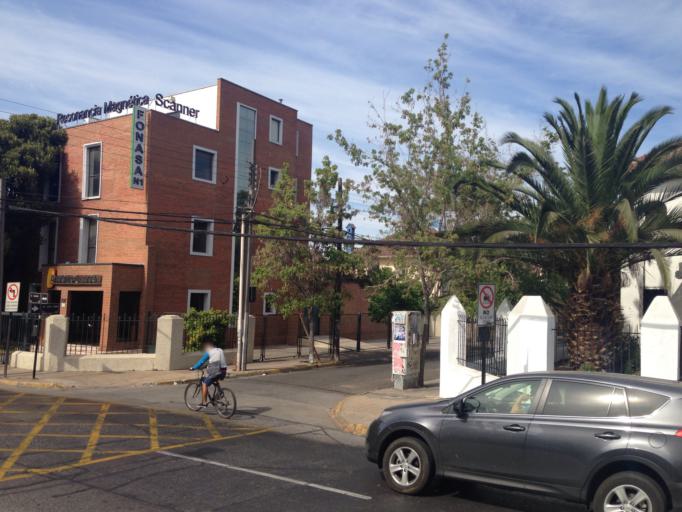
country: CL
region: Santiago Metropolitan
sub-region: Provincia de Santiago
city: Santiago
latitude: -33.4402
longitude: -70.6245
